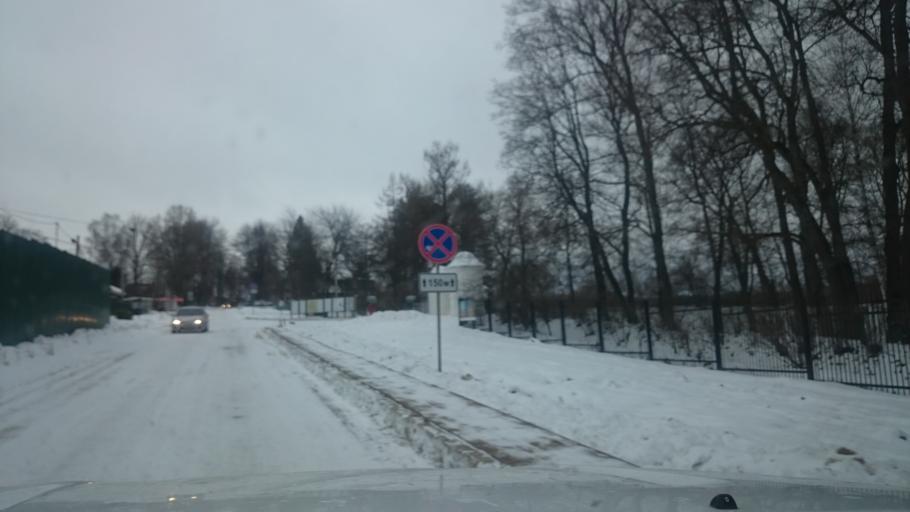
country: RU
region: Tula
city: Pervomayskiy
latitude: 54.0734
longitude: 37.5310
